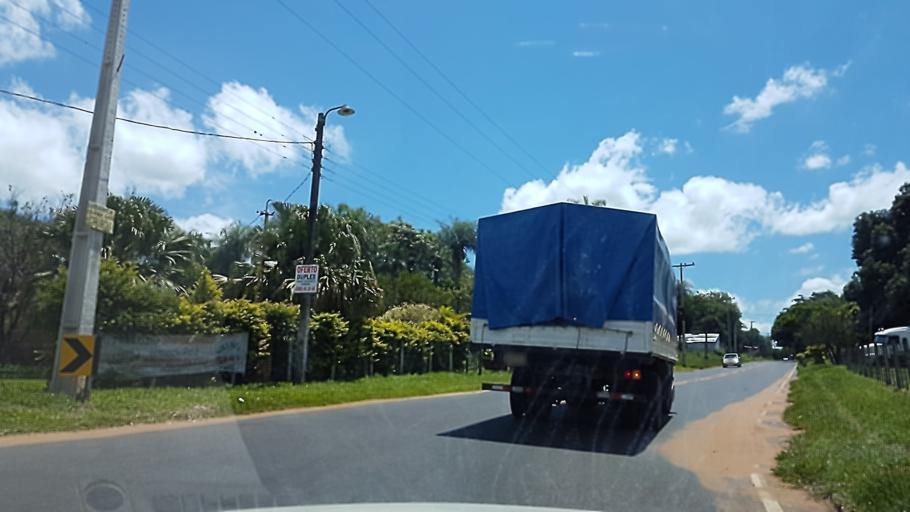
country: PY
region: Central
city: San Lorenzo
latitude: -25.3097
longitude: -57.4686
